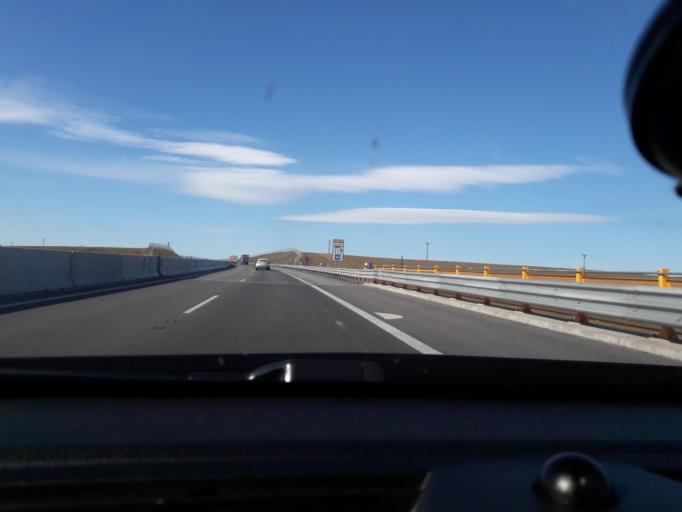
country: SK
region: Banskobystricky
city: Hrochot,Slovakia
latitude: 48.5647
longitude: 19.3110
